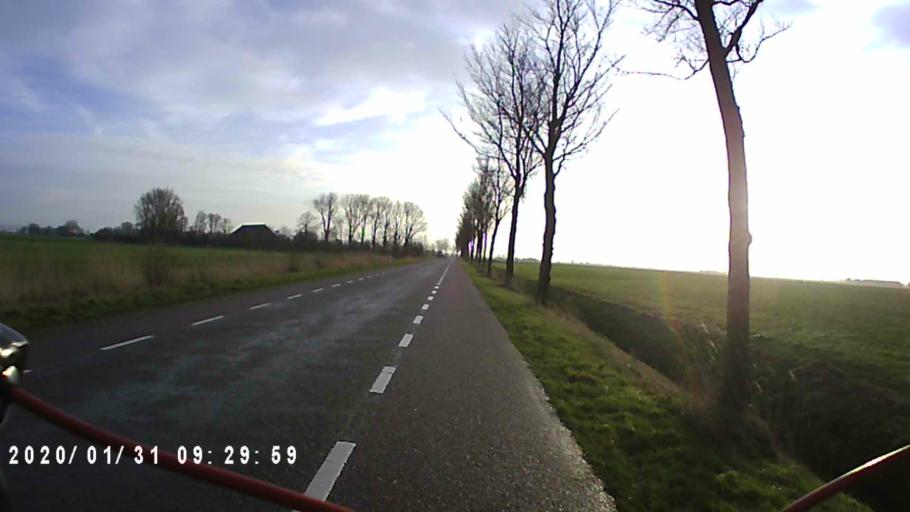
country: NL
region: Groningen
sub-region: Gemeente Zuidhorn
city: Aduard
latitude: 53.3046
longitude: 6.4519
